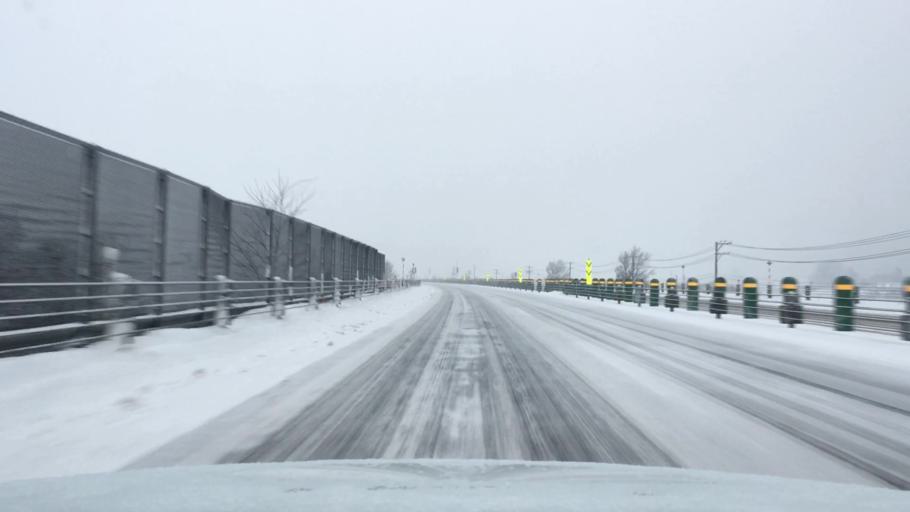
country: JP
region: Akita
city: Hanawa
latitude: 40.2902
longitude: 140.7581
